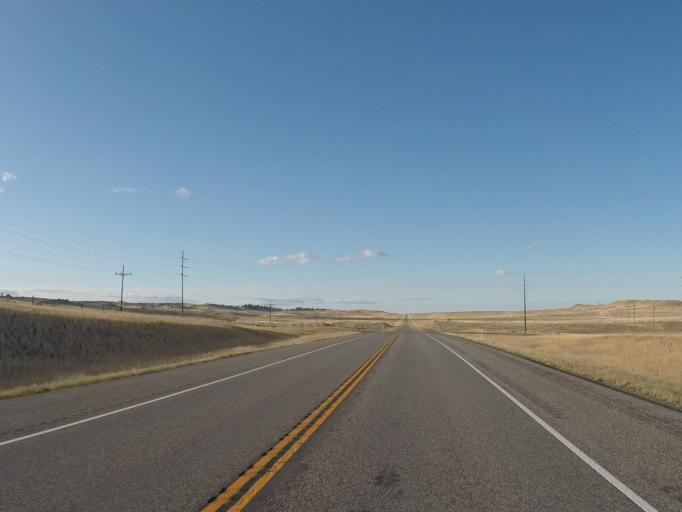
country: US
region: Montana
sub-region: Golden Valley County
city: Ryegate
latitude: 46.2181
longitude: -108.9263
